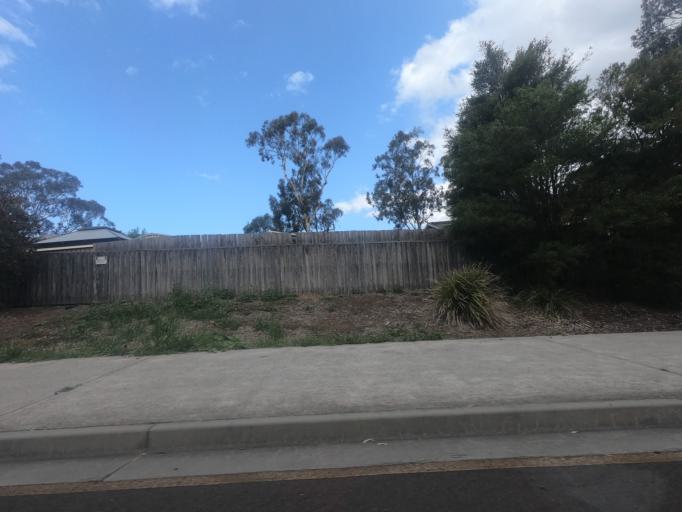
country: AU
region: New South Wales
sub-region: Wollongong
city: Dapto
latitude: -34.4909
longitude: 150.7652
